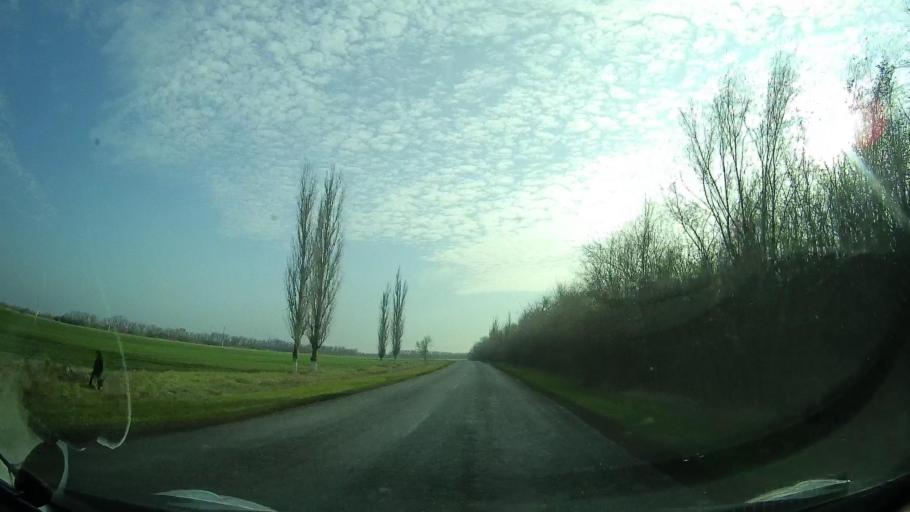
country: RU
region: Rostov
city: Mechetinskaya
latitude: 46.8214
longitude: 40.5550
